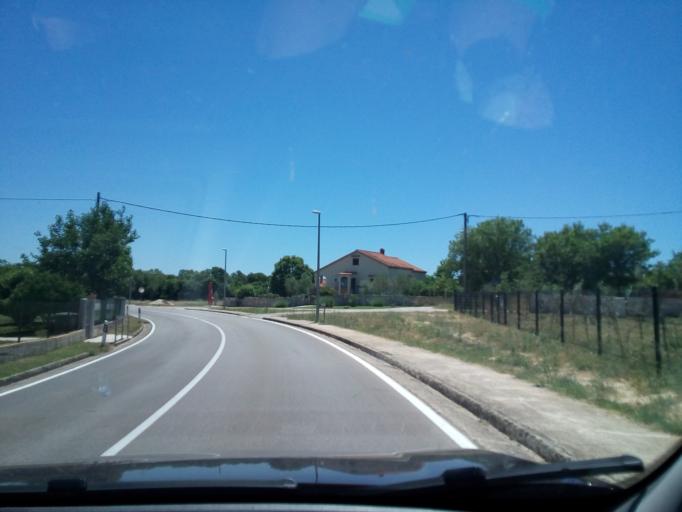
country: HR
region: Zadarska
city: Zadar
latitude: 44.1737
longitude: 15.2886
